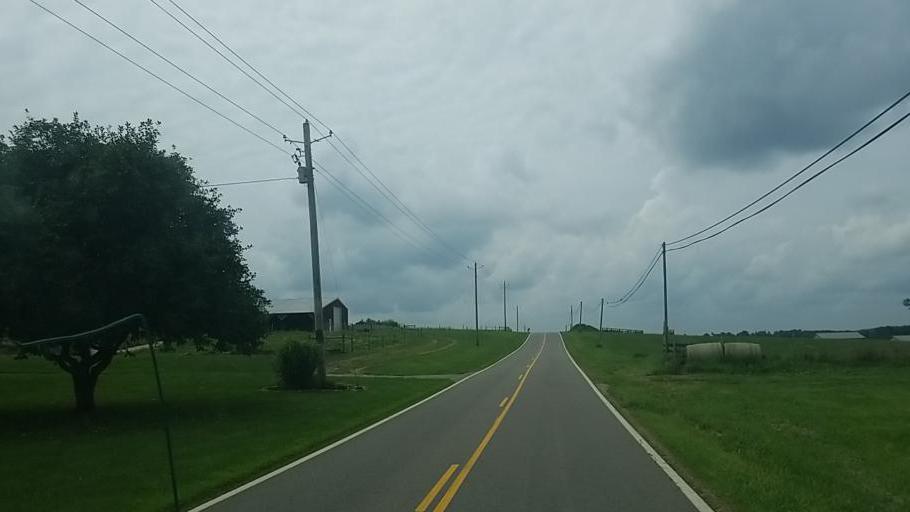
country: US
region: Ohio
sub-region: Licking County
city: Utica
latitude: 40.2014
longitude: -82.3465
